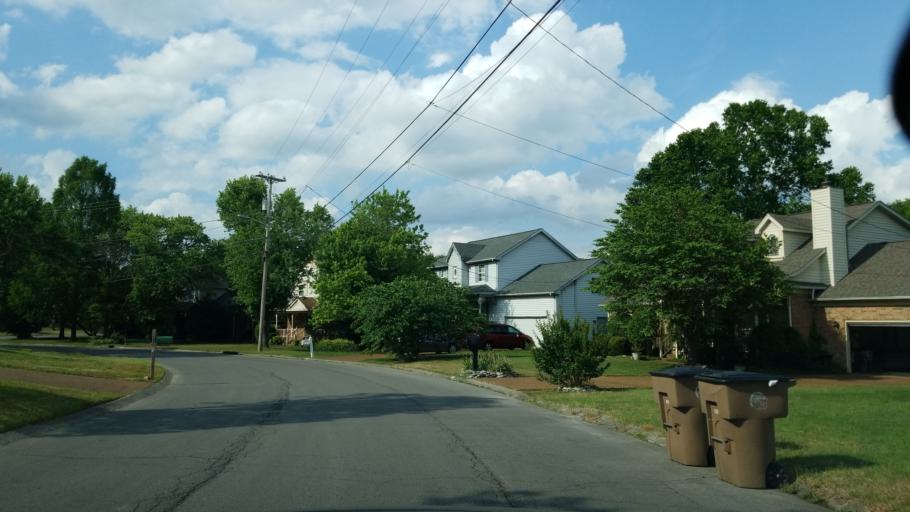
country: US
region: Tennessee
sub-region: Rutherford County
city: La Vergne
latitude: 36.0778
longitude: -86.5969
